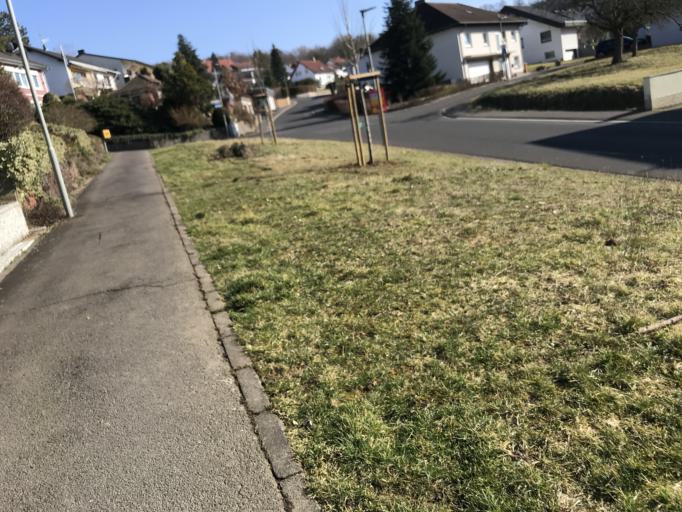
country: DE
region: Hesse
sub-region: Regierungsbezirk Darmstadt
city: Nidda
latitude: 50.4065
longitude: 9.0120
